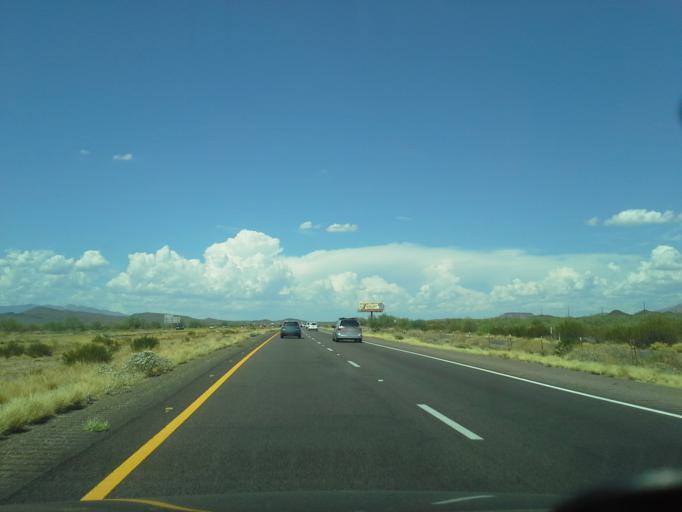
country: US
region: Arizona
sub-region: Maricopa County
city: Anthem
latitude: 33.8852
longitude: -112.1475
